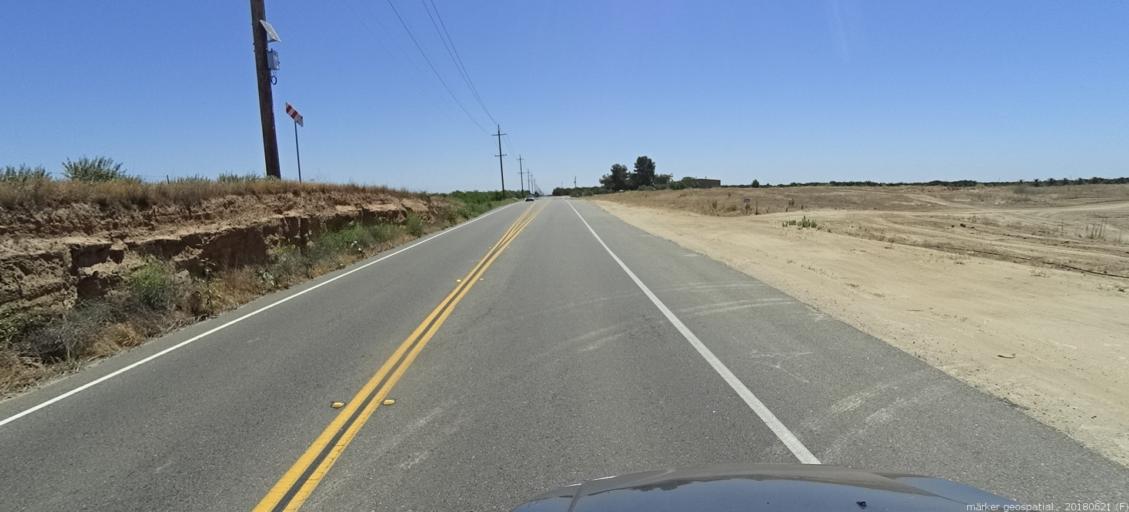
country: US
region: California
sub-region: Madera County
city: Bonadelle Ranchos-Madera Ranchos
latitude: 36.8804
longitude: -119.8961
